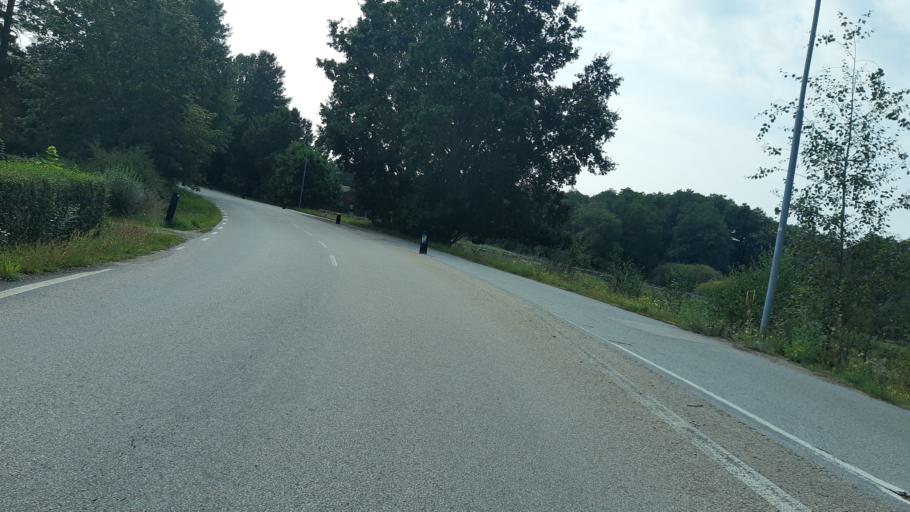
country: SE
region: Blekinge
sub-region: Karlskrona Kommun
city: Nattraby
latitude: 56.2243
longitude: 15.4141
